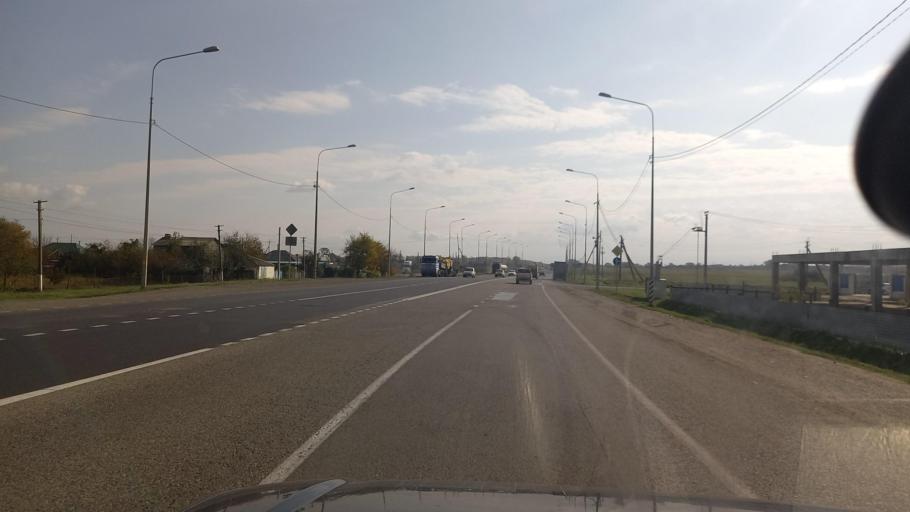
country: RU
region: Krasnodarskiy
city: Novoukrainskiy
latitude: 44.8943
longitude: 38.0618
